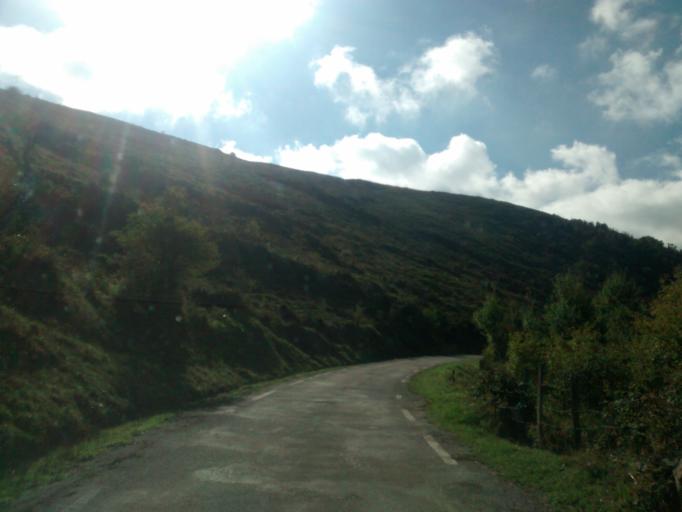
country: ES
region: Castille and Leon
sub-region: Provincia de Burgos
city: Arija
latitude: 42.9332
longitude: -4.0290
